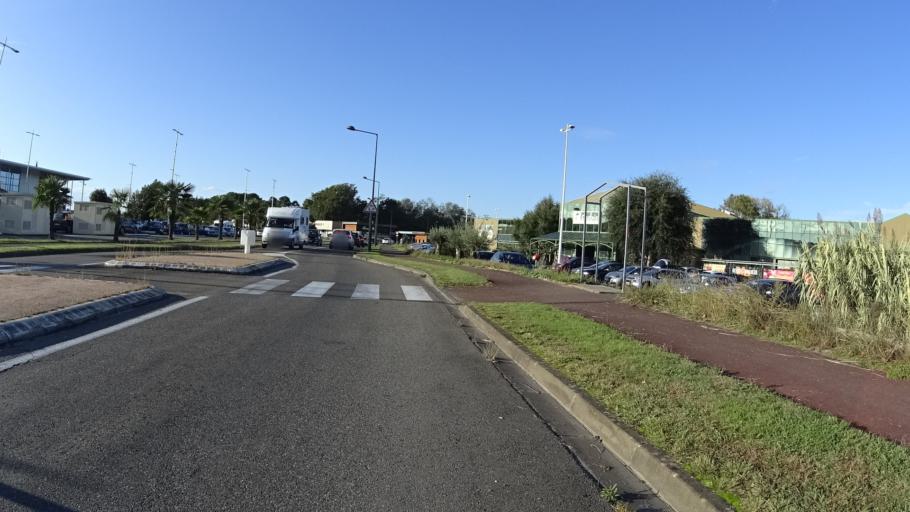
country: FR
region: Aquitaine
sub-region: Departement des Landes
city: Saint-Paul-les-Dax
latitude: 43.7305
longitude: -1.0386
